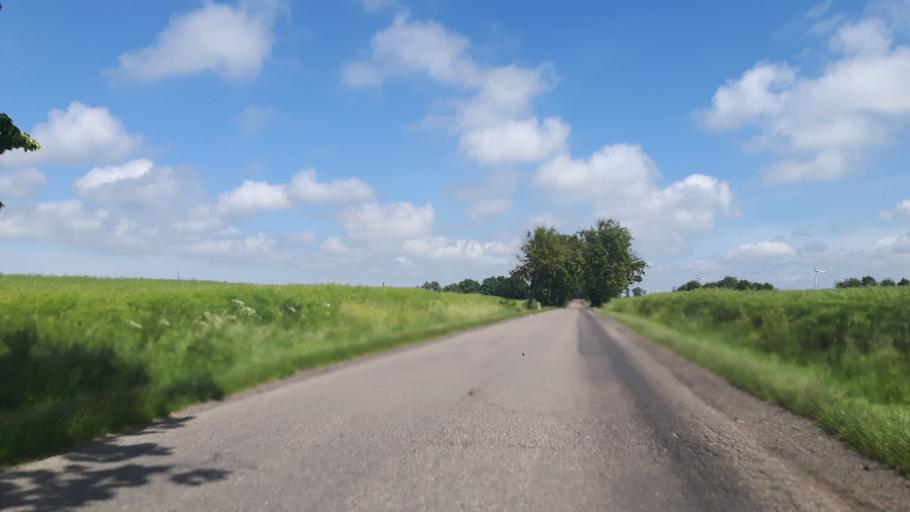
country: PL
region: Pomeranian Voivodeship
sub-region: Powiat slupski
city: Ustka
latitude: 54.5229
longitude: 16.7877
